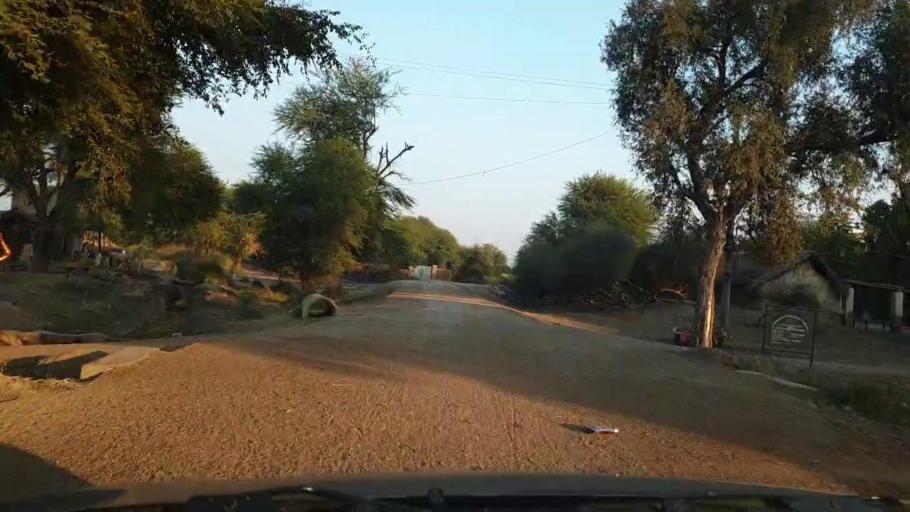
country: PK
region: Sindh
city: Jhol
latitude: 25.9126
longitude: 68.9355
